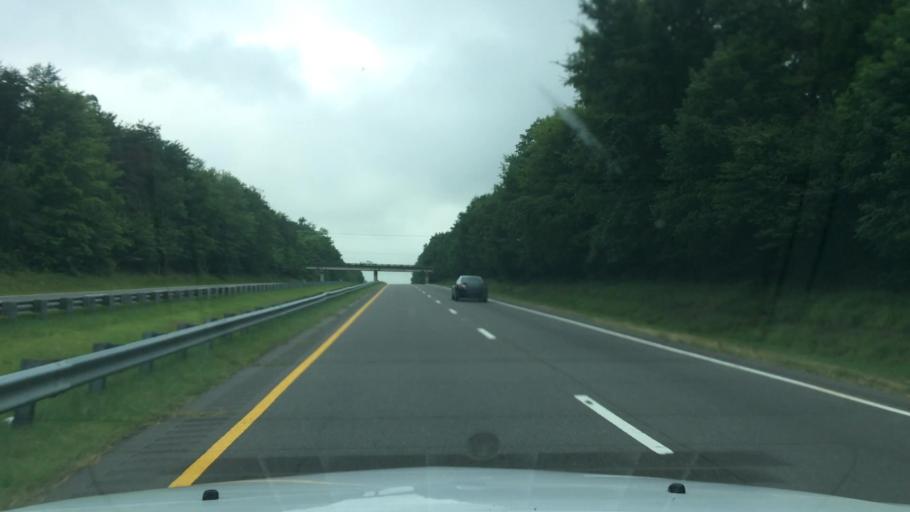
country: US
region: North Carolina
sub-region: Forsyth County
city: Lewisville
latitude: 36.1017
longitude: -80.4861
